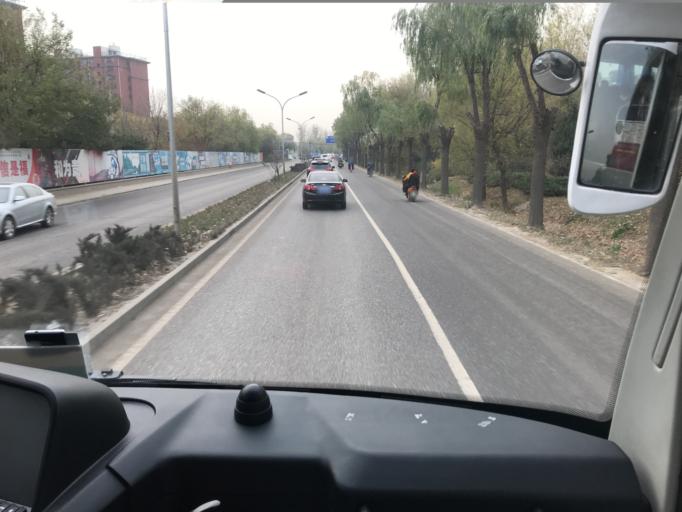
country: CN
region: Beijing
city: Sujiatuo
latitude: 40.0939
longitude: 116.2086
